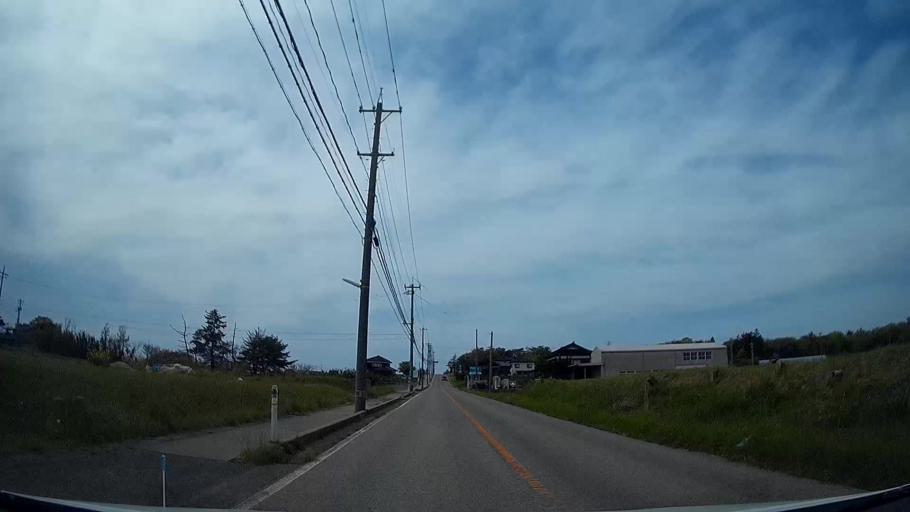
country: JP
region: Ishikawa
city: Hakui
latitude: 37.0149
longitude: 136.7542
